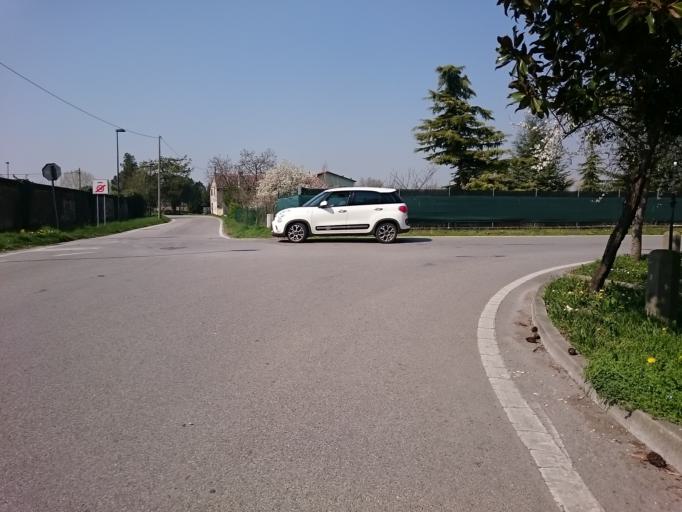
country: IT
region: Veneto
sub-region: Provincia di Padova
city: Este
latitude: 45.2080
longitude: 11.6503
